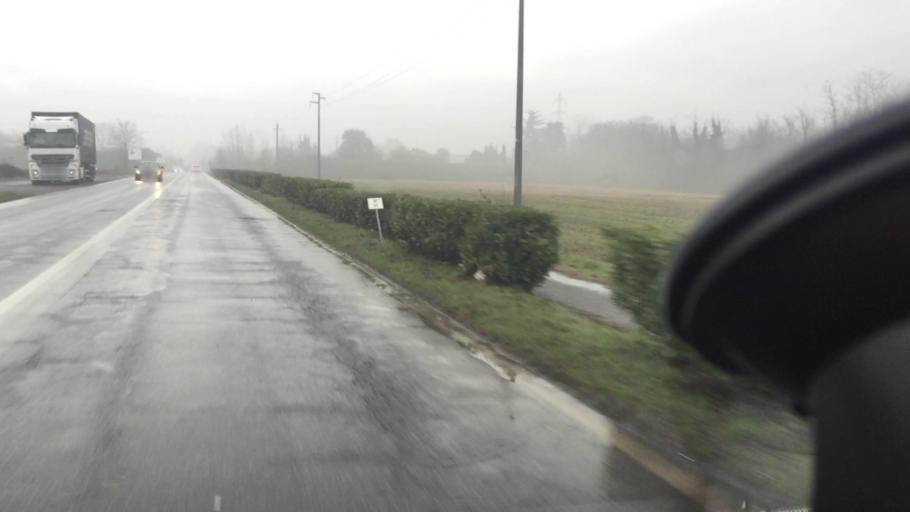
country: IT
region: Lombardy
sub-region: Citta metropolitana di Milano
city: Trezzo sull'Adda
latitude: 45.5940
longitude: 9.5224
